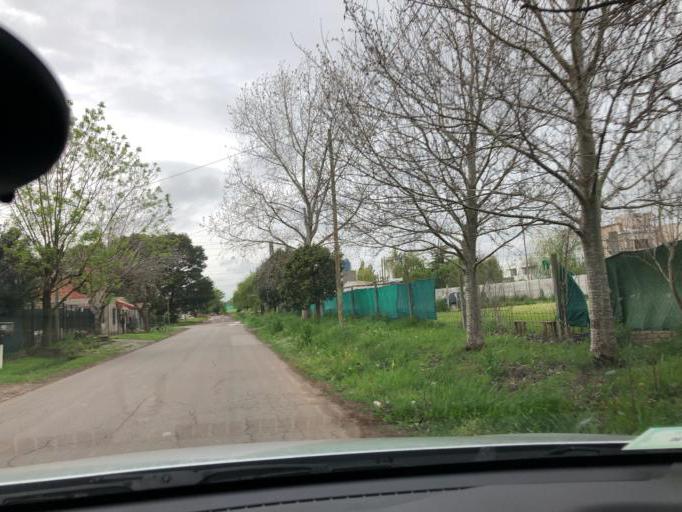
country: AR
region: Buenos Aires
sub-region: Partido de La Plata
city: La Plata
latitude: -34.8925
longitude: -58.0539
